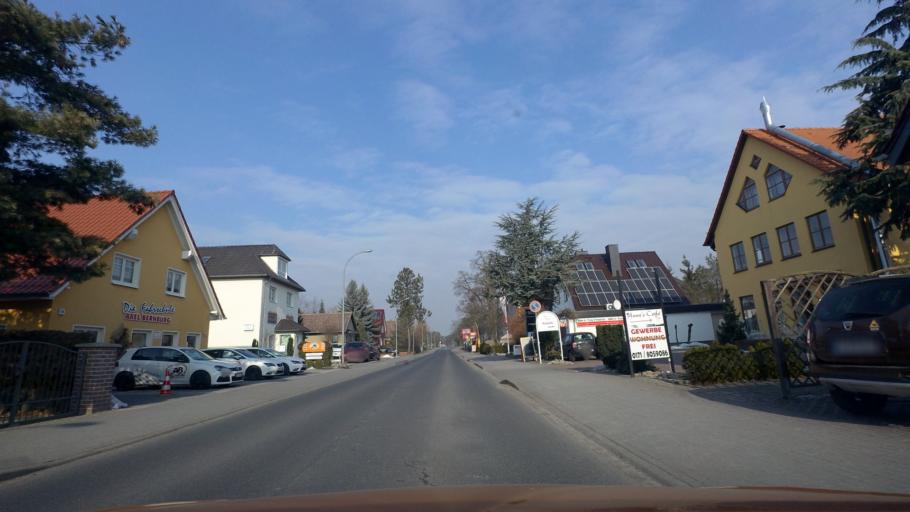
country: DE
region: Brandenburg
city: Ludwigsfelde
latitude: 52.3052
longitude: 13.2579
